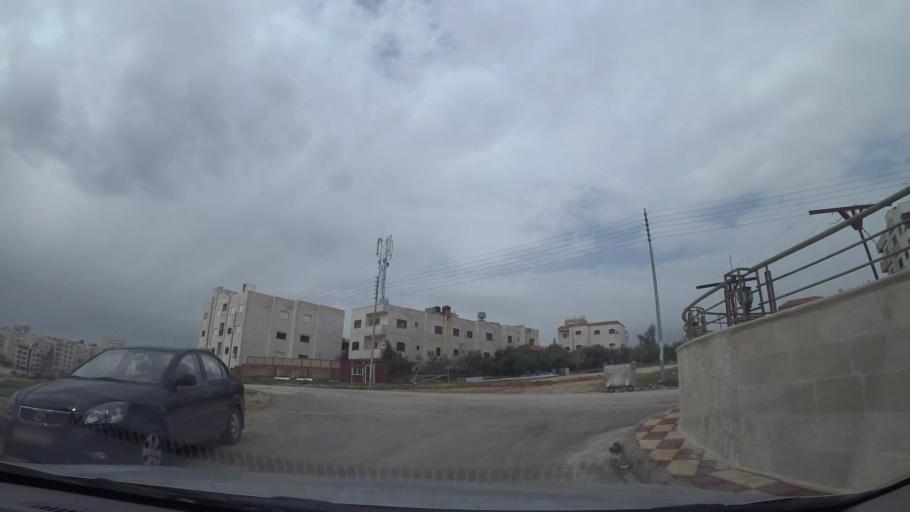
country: JO
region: Amman
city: Umm as Summaq
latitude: 31.9037
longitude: 35.8395
